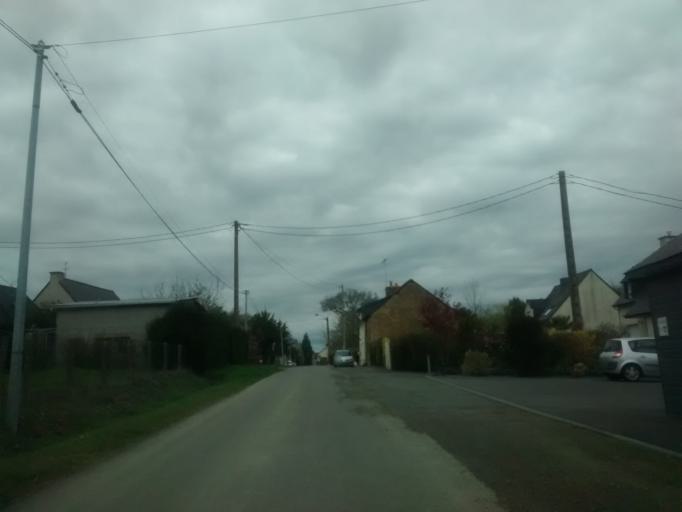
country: FR
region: Brittany
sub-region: Departement d'Ille-et-Vilaine
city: Erce-pres-Liffre
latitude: 48.2414
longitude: -1.5024
